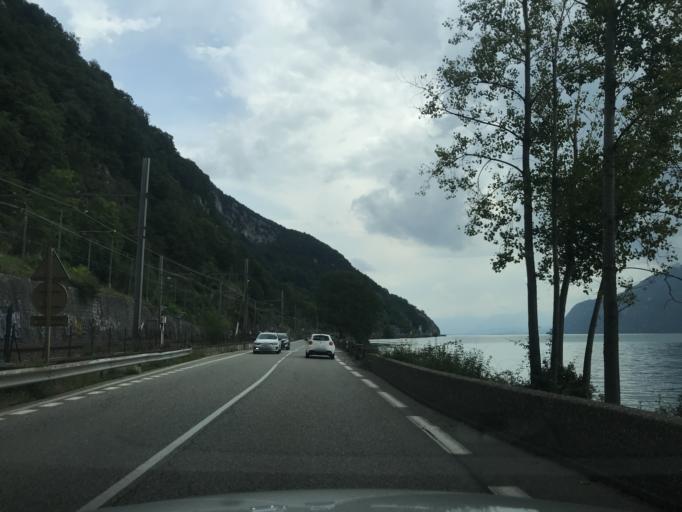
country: FR
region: Rhone-Alpes
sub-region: Departement de la Savoie
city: Chatillon
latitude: 45.7701
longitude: 5.8690
